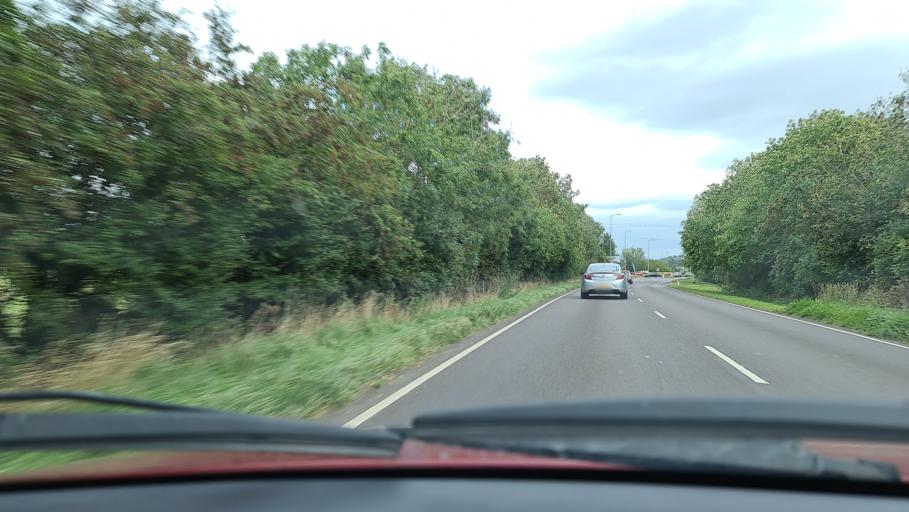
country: GB
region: England
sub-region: Oxfordshire
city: Somerton
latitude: 51.9596
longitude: -1.2060
